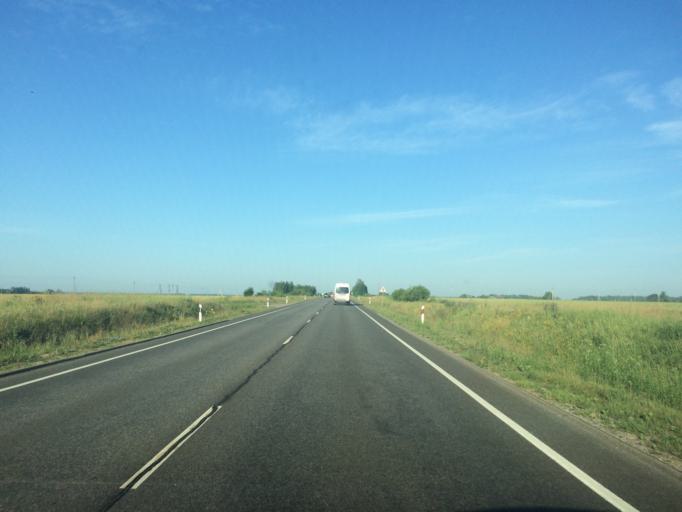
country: LT
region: Vilnius County
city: Ukmerge
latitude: 55.2130
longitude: 24.6571
